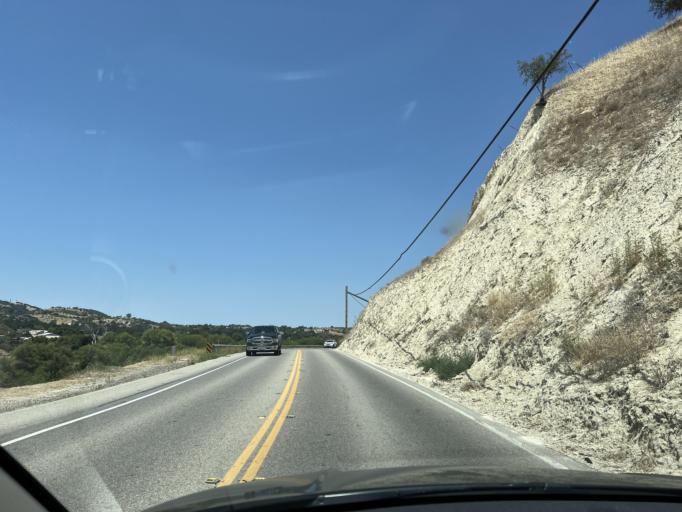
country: US
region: California
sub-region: San Luis Obispo County
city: Paso Robles
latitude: 35.6246
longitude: -120.6807
